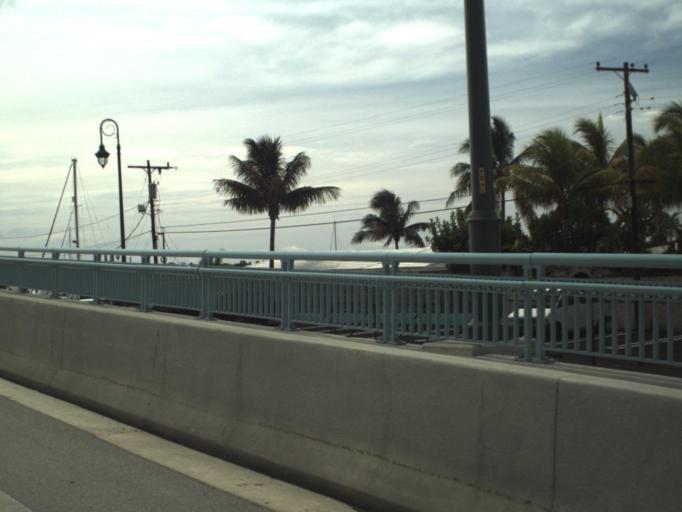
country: US
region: Florida
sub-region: Palm Beach County
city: Riviera Beach
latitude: 26.7831
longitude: -80.0490
